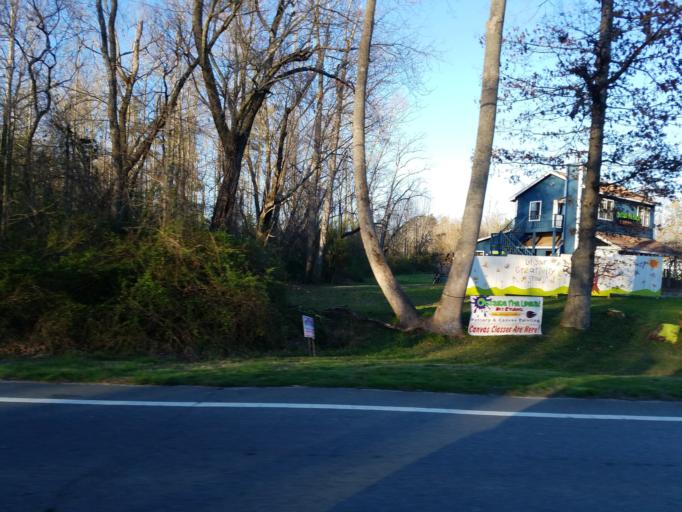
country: US
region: Georgia
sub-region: Dawson County
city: Dawsonville
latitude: 34.4141
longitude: -84.1106
